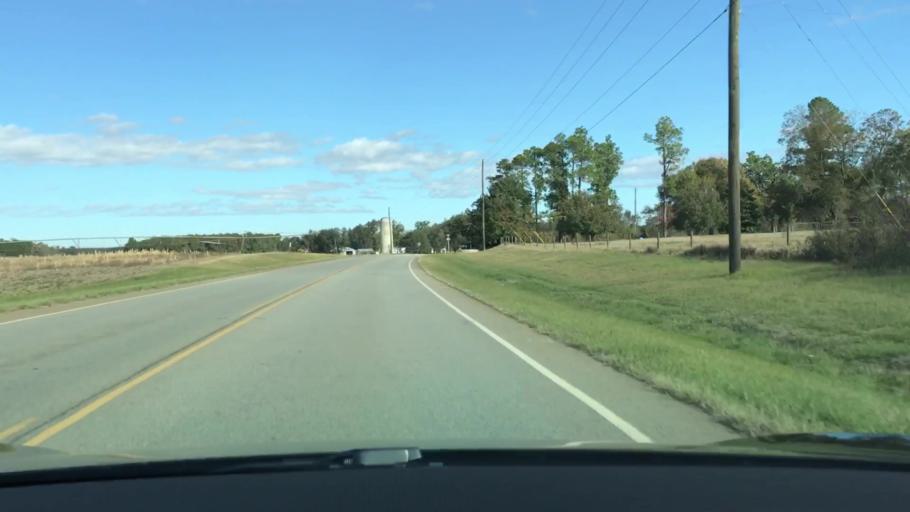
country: US
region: Georgia
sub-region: Jefferson County
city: Wrens
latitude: 33.1508
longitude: -82.4573
